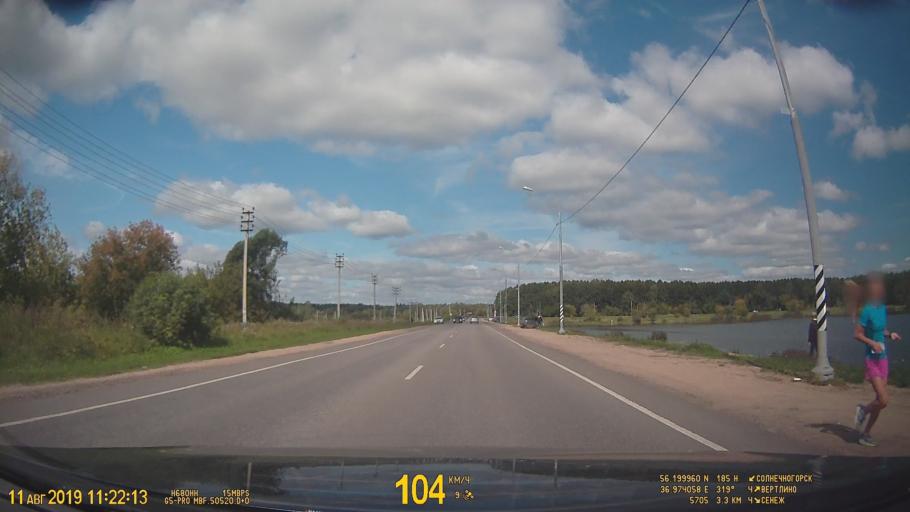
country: RU
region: Moskovskaya
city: Solnechnogorsk
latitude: 56.2003
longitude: 36.9736
